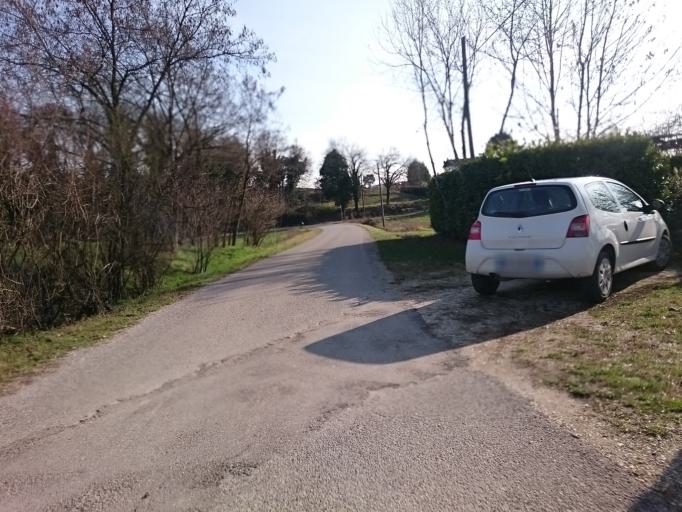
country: IT
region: Veneto
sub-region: Provincia di Verona
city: Salionze
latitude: 45.4154
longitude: 10.7109
